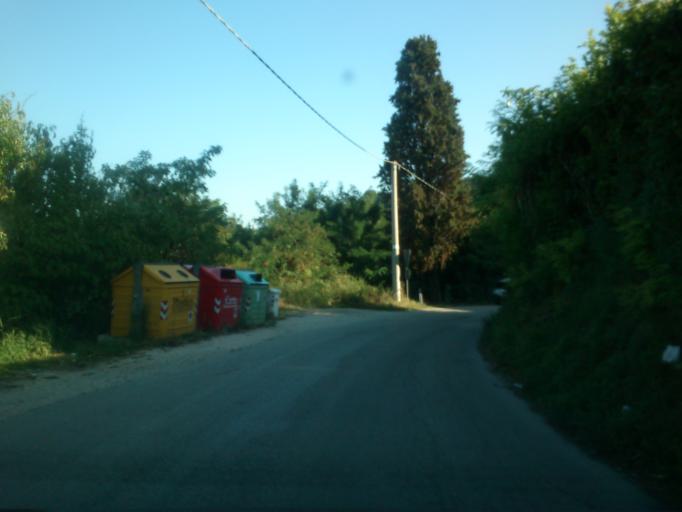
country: IT
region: The Marches
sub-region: Provincia di Pesaro e Urbino
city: Mombaroccio
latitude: 43.7967
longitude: 12.8659
